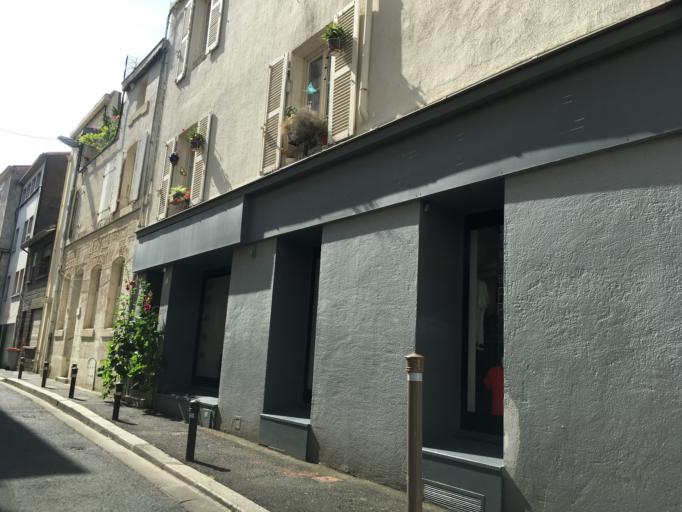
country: FR
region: Poitou-Charentes
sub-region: Departement des Deux-Sevres
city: Niort
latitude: 46.3237
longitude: -0.4632
